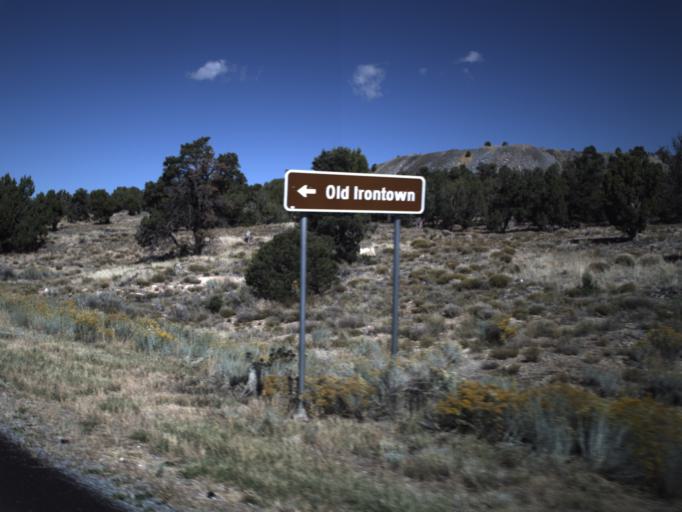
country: US
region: Utah
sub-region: Washington County
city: Enterprise
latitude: 37.6143
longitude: -113.4061
